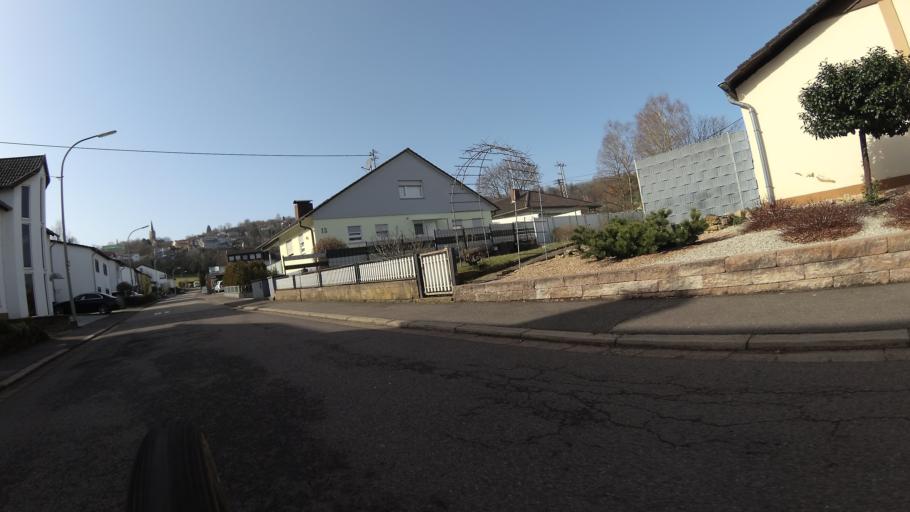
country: DE
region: Saarland
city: Wallerfangen
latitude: 49.2929
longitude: 6.6988
